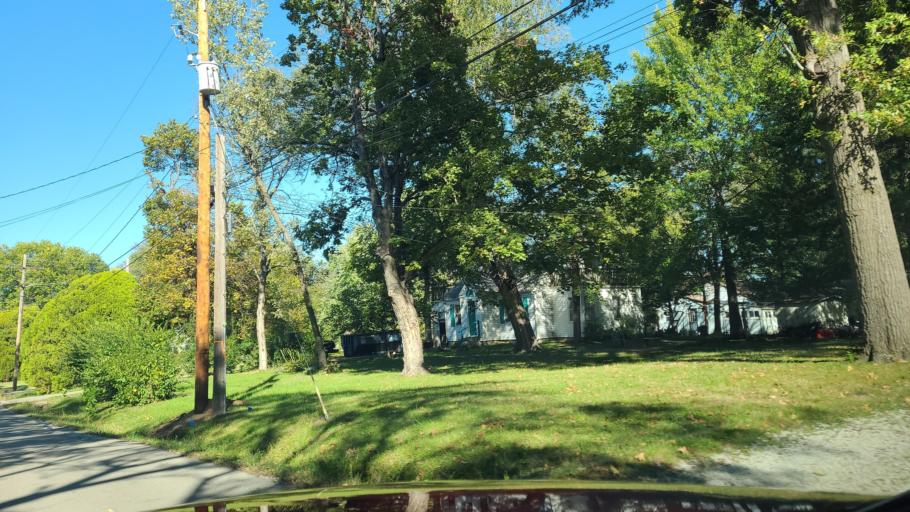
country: US
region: Kansas
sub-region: Douglas County
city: Lawrence
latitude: 38.9468
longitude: -95.2306
